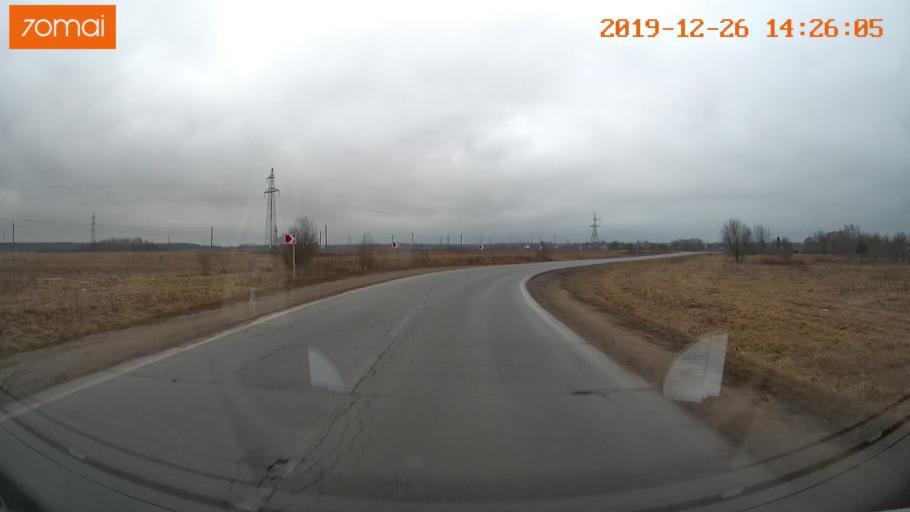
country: RU
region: Jaroslavl
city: Poshekhon'ye
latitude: 58.4889
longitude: 39.0914
